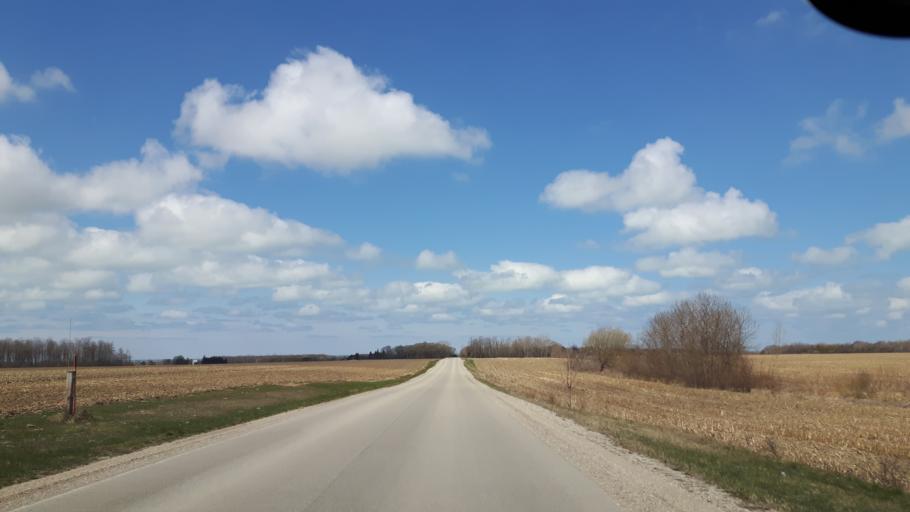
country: CA
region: Ontario
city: Goderich
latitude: 43.6985
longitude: -81.6866
